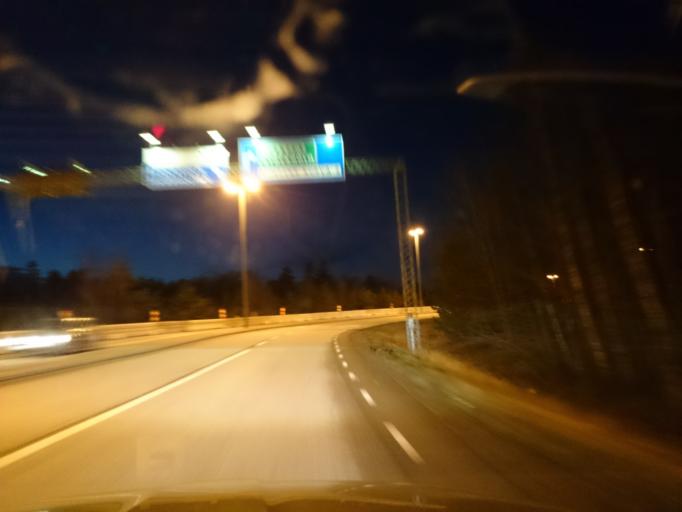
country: SE
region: Stockholm
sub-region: Huddinge Kommun
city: Segeltorp
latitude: 59.2650
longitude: 17.8949
